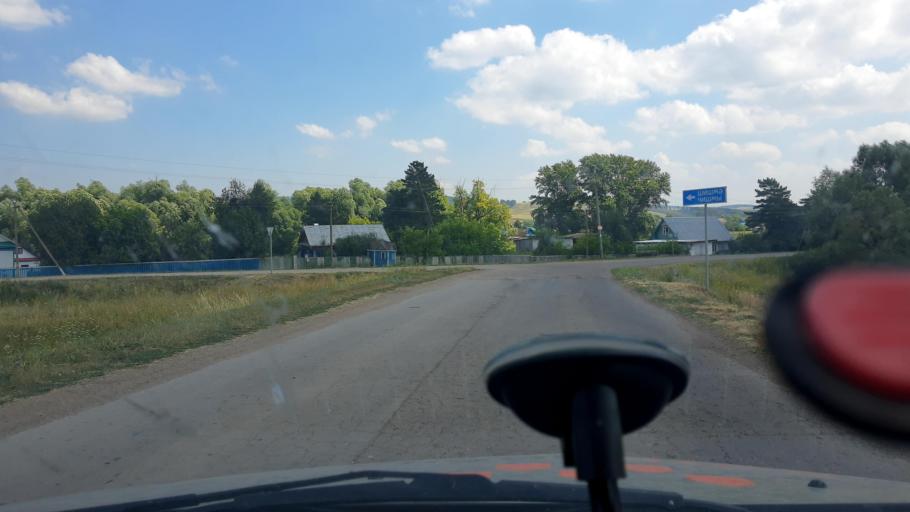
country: RU
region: Bashkortostan
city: Chekmagush
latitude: 54.8827
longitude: 54.6041
